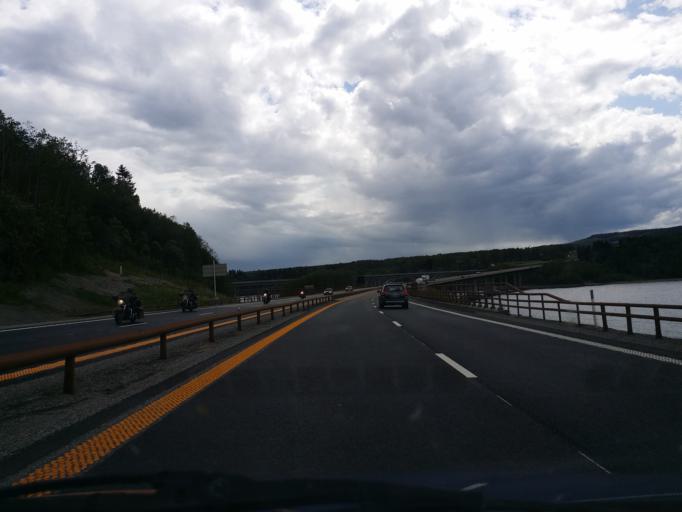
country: NO
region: Akershus
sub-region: Eidsvoll
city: Eidsvoll
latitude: 60.4043
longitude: 11.2370
